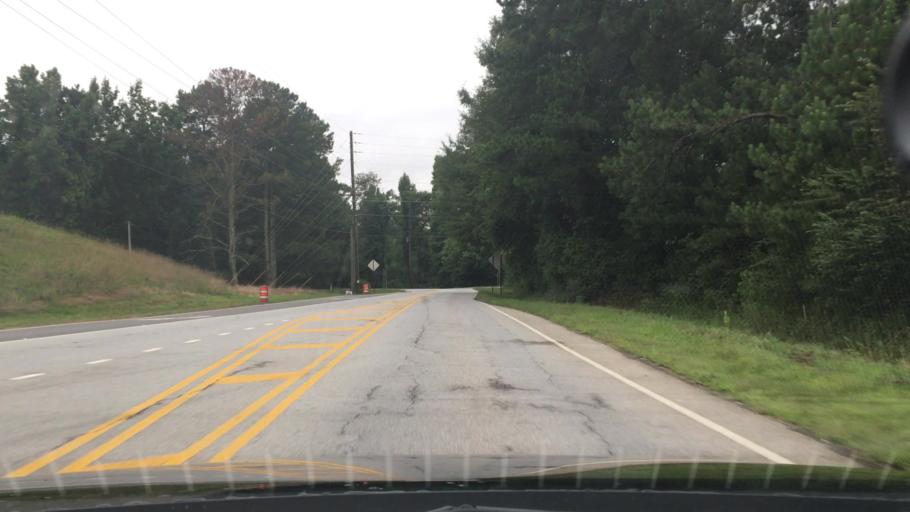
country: US
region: Georgia
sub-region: Fayette County
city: Peachtree City
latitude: 33.3971
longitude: -84.6231
